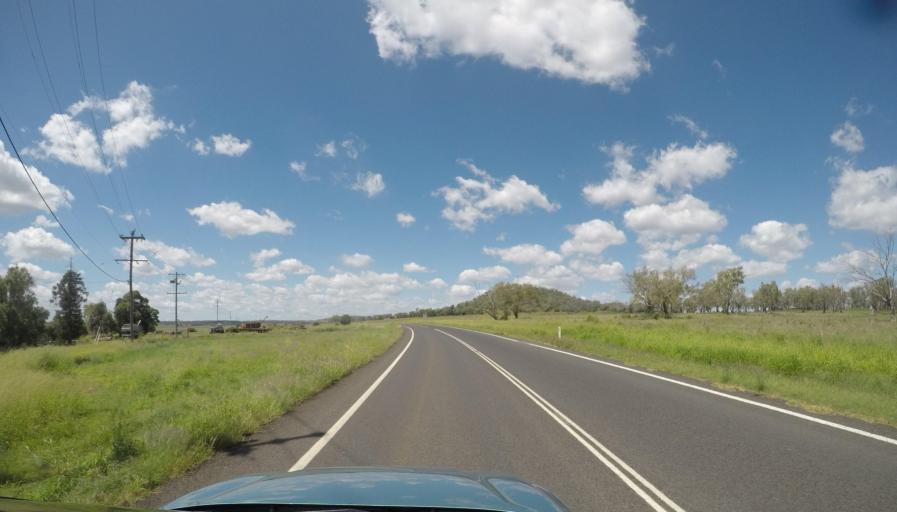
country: AU
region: Queensland
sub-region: Toowoomba
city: Oakey
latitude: -27.5394
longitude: 151.6326
